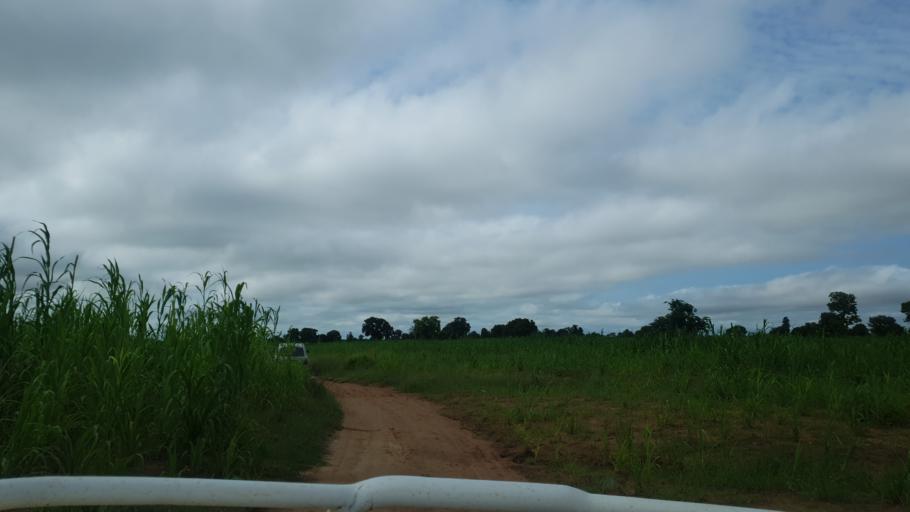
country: ML
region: Segou
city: Baroueli
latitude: 13.4951
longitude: -6.8967
